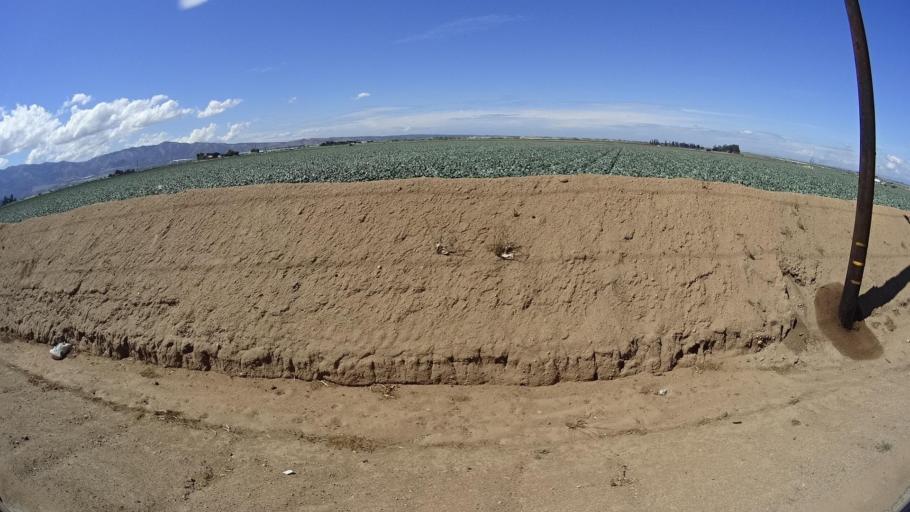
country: US
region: California
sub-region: Monterey County
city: Chualar
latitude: 36.6417
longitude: -121.5426
